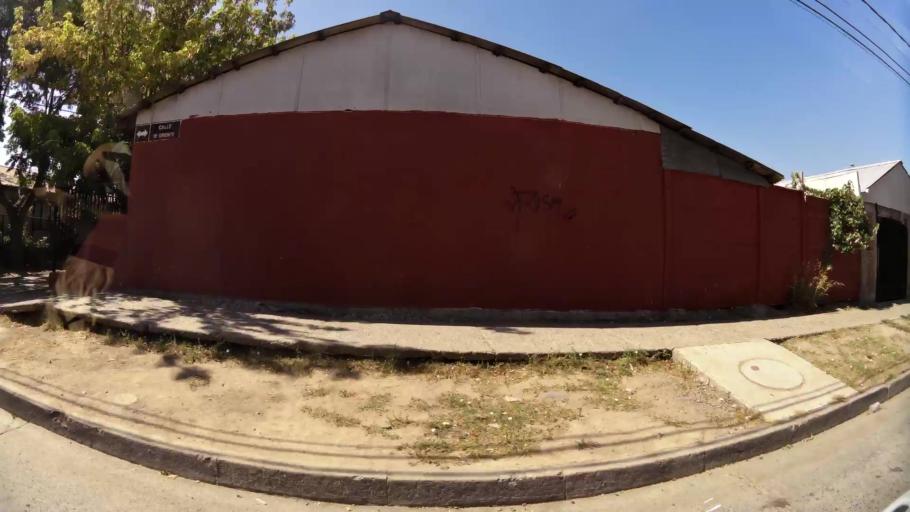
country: CL
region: Maule
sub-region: Provincia de Talca
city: Talca
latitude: -35.4174
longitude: -71.6390
